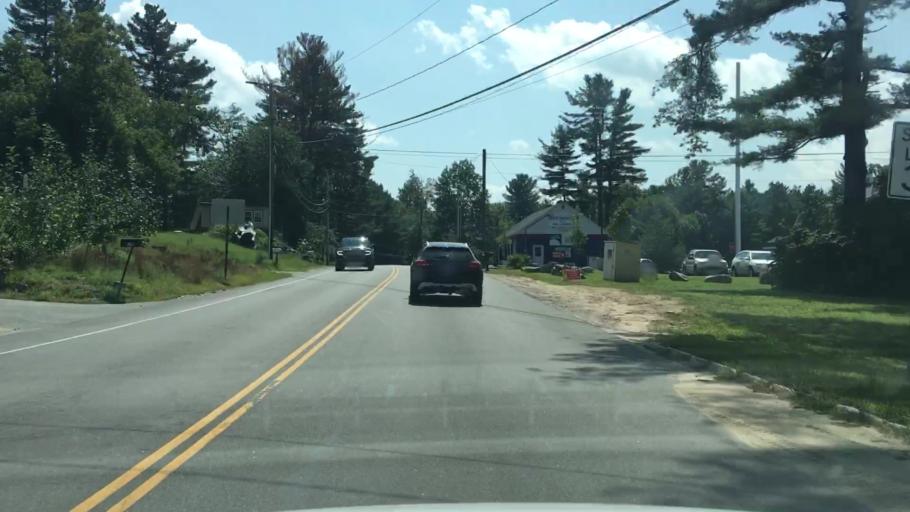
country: US
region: New Hampshire
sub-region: Rockingham County
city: Windham
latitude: 42.8022
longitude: -71.3518
